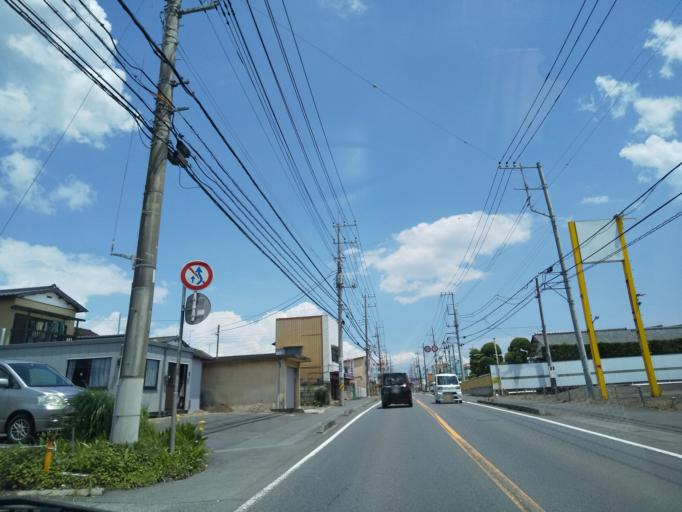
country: JP
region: Ibaraki
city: Ishioka
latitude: 36.1869
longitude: 140.2944
